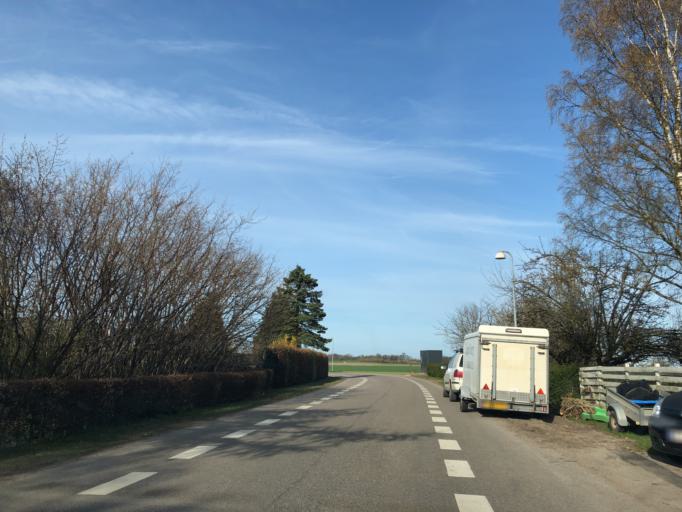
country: DK
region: Zealand
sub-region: Stevns Kommune
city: Store Heddinge
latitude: 55.2819
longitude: 12.4400
